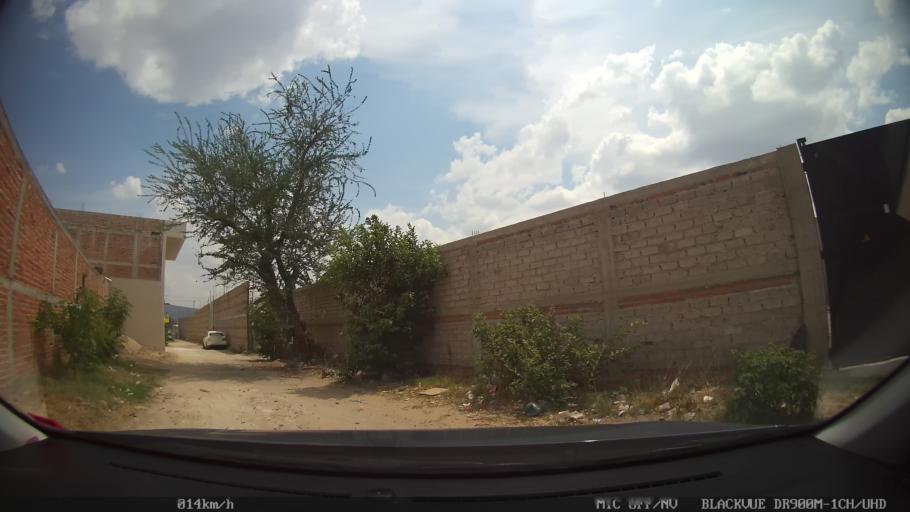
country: MX
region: Jalisco
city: Tonala
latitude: 20.6822
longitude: -103.2370
